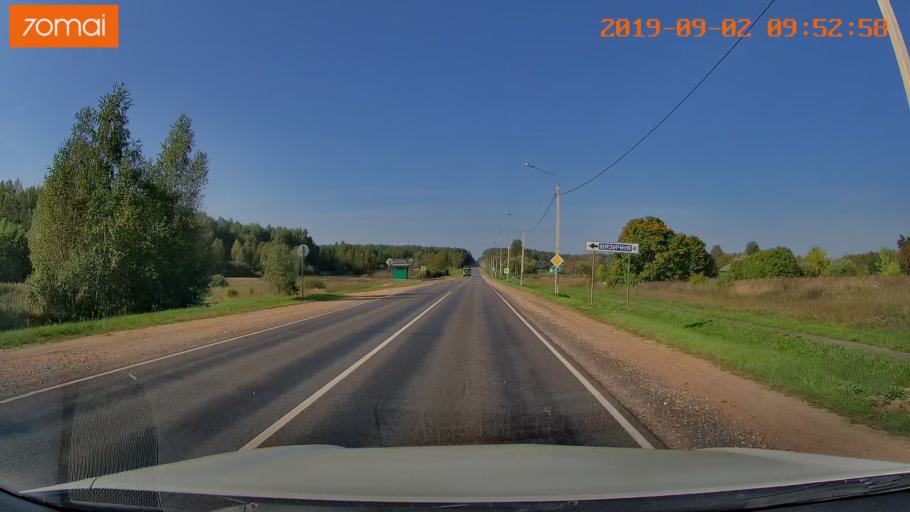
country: RU
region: Kaluga
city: Mosal'sk
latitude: 54.5868
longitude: 34.6821
